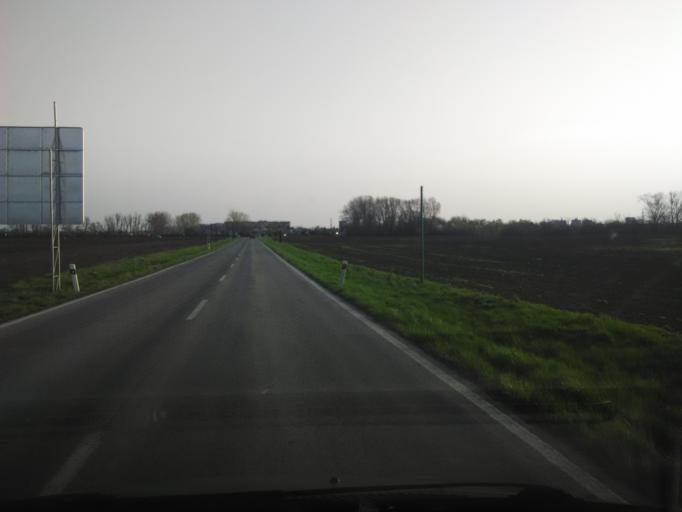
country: SK
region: Trnavsky
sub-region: Okres Galanta
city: Galanta
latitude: 48.1819
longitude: 17.7069
